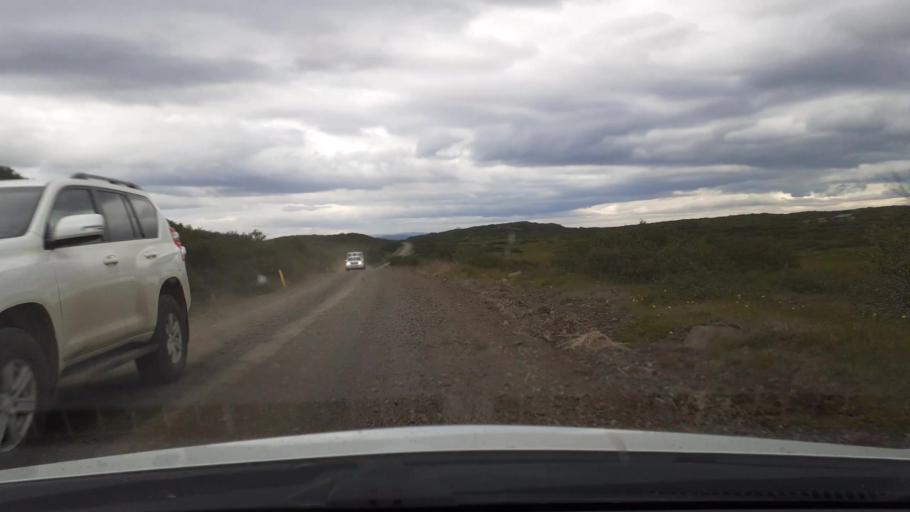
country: IS
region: West
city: Borgarnes
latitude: 64.5971
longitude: -21.9804
